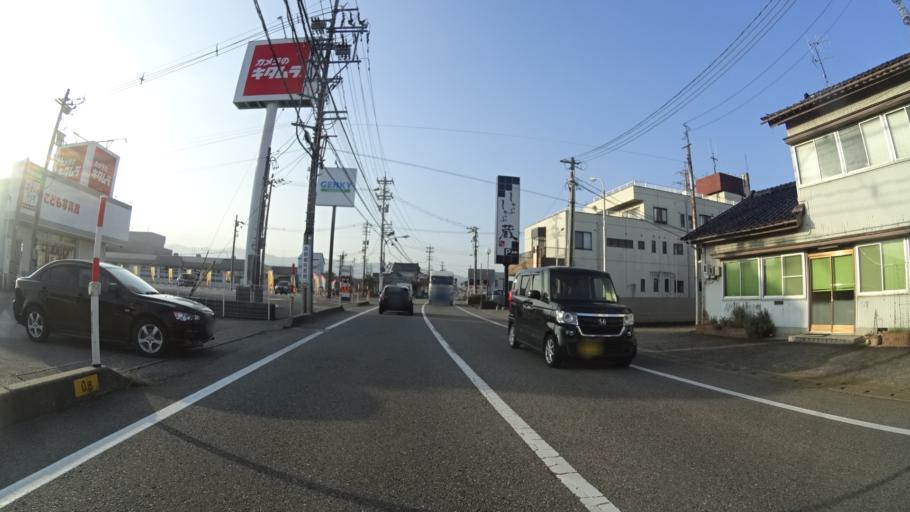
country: JP
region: Ishikawa
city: Nanao
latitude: 37.0349
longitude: 136.9686
